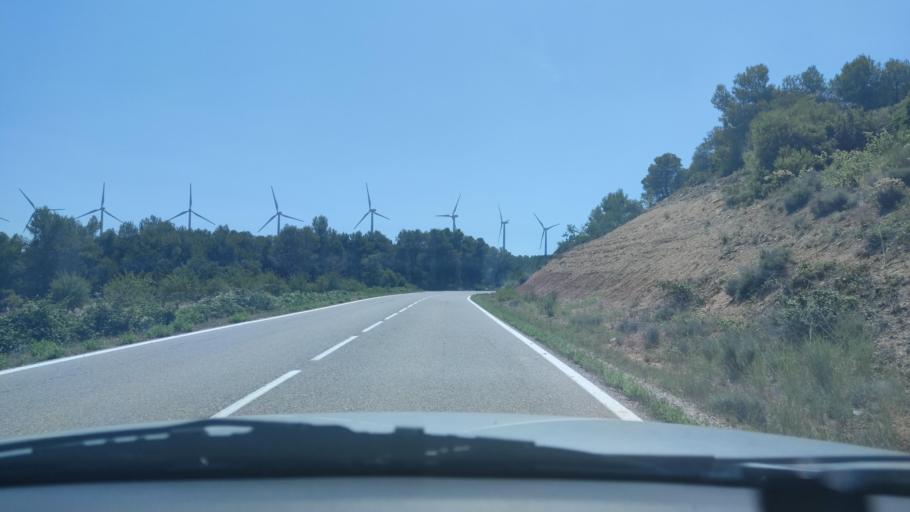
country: ES
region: Catalonia
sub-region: Provincia de Lleida
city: Fulleda
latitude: 41.4465
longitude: 1.0382
